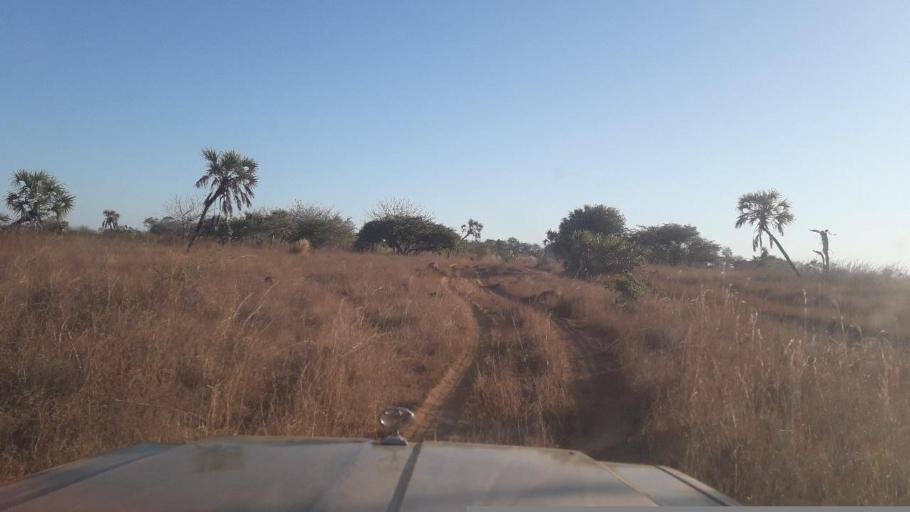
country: MG
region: Boeny
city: Sitampiky
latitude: -16.4991
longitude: 45.6045
